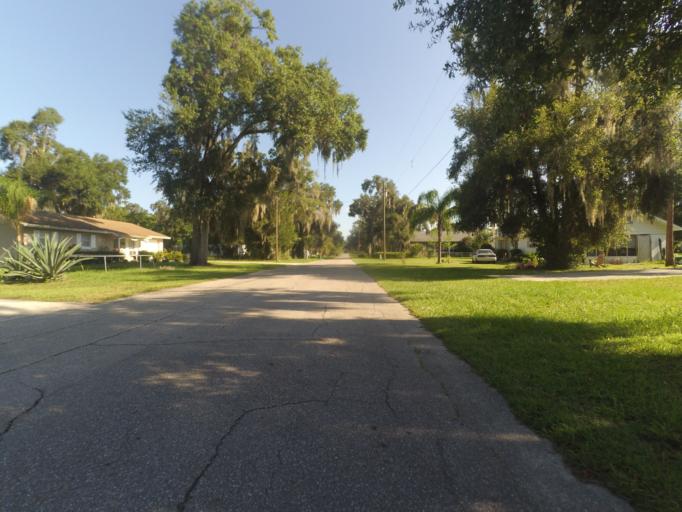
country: US
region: Florida
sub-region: Lake County
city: Umatilla
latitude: 28.9319
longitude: -81.6694
